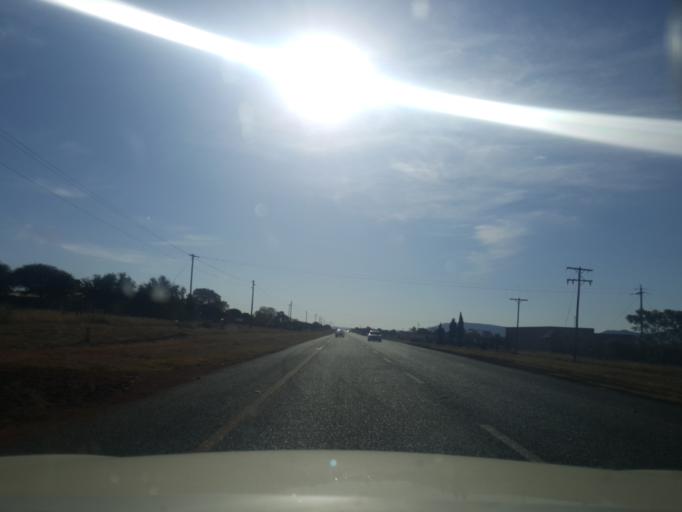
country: ZA
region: North-West
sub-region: Ngaka Modiri Molema District Municipality
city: Zeerust
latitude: -25.4841
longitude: 25.9157
